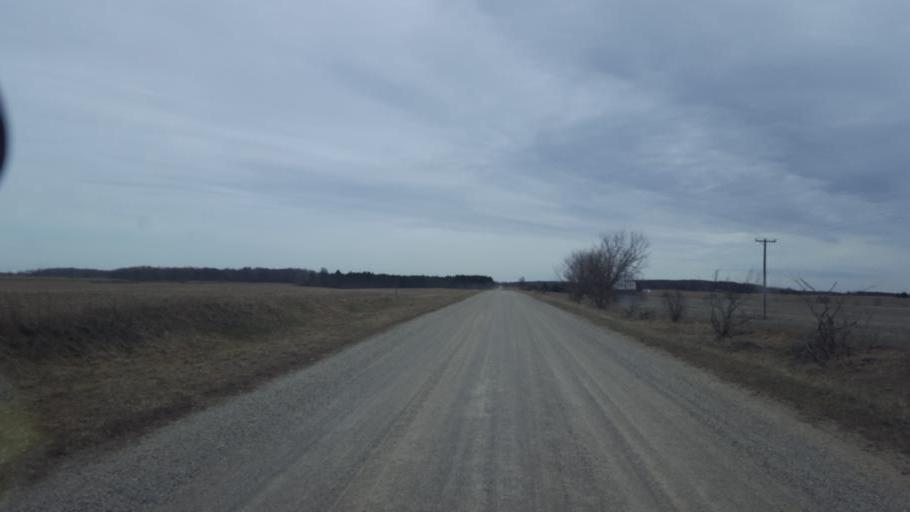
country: US
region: Michigan
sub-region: Montcalm County
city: Edmore
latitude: 43.4514
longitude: -85.0375
